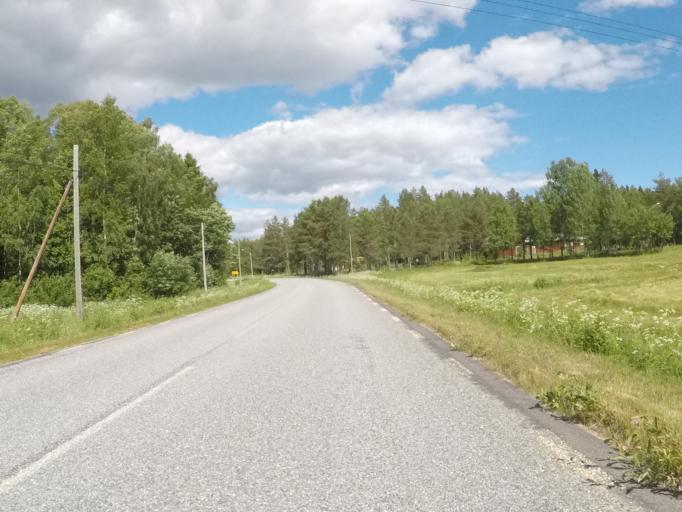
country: SE
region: Vaesterbotten
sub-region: Robertsfors Kommun
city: Robertsfors
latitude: 63.9658
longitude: 20.8115
